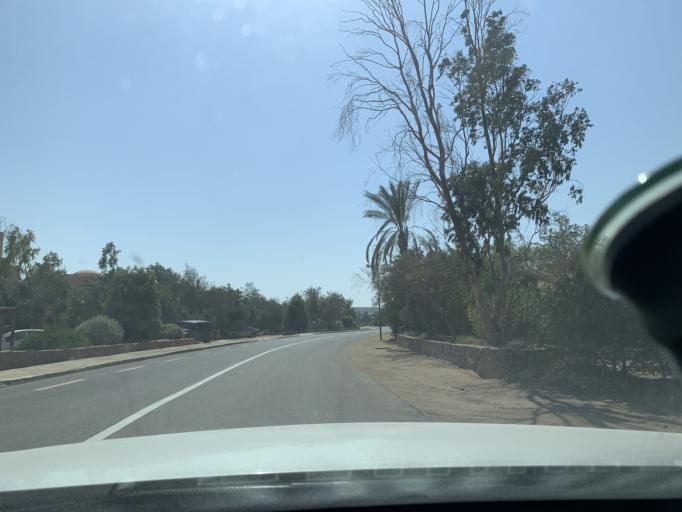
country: EG
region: Red Sea
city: El Gouna
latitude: 27.4033
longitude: 33.6752
